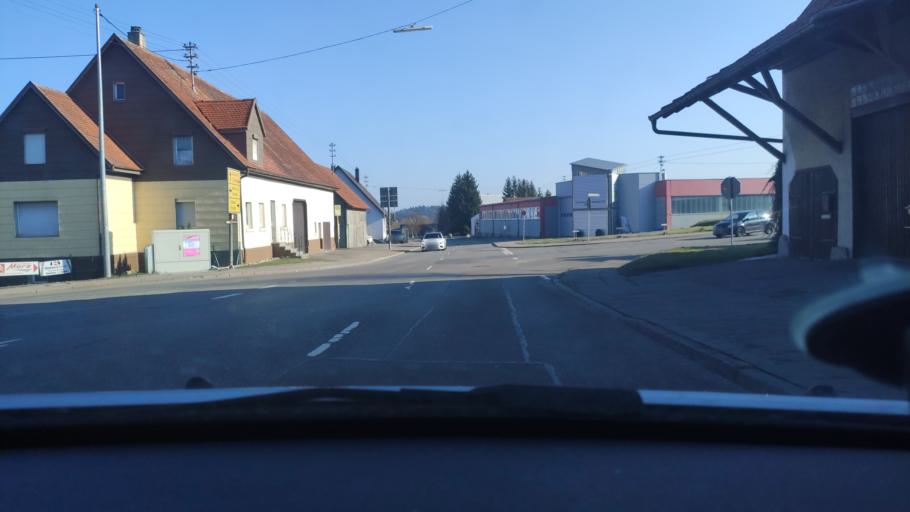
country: DE
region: Baden-Wuerttemberg
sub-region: Tuebingen Region
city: Balingen
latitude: 48.2418
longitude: 8.8538
